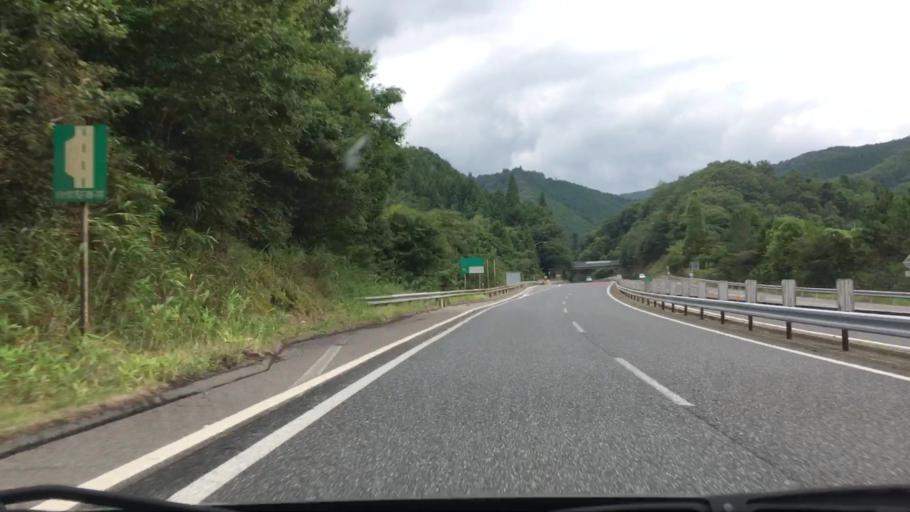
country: JP
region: Okayama
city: Niimi
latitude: 35.0102
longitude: 133.5012
